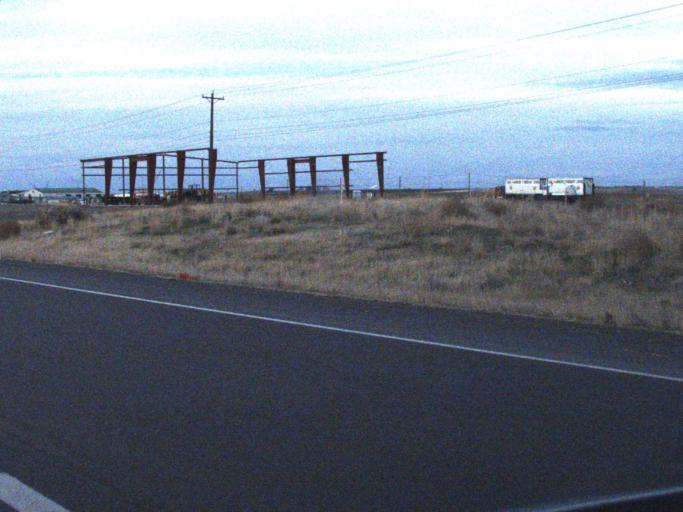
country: US
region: Washington
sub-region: Franklin County
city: Pasco
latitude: 46.2449
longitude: -119.0645
